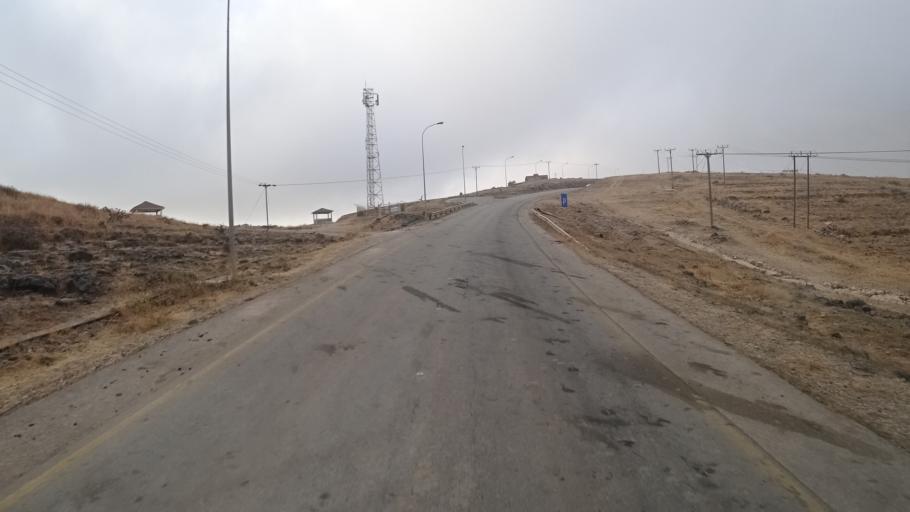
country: OM
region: Zufar
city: Salalah
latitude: 17.1212
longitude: 53.9766
